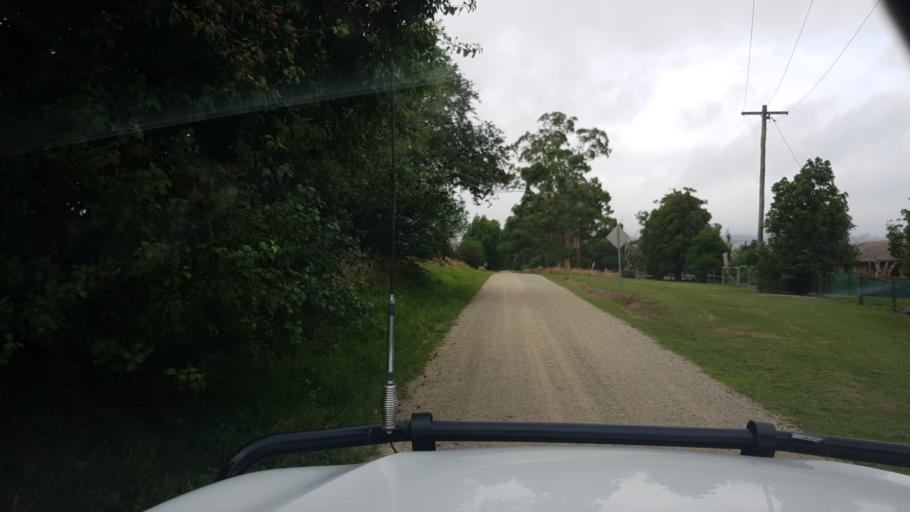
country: AU
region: Victoria
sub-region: Baw Baw
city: Warragul
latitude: -38.2299
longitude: 145.9721
